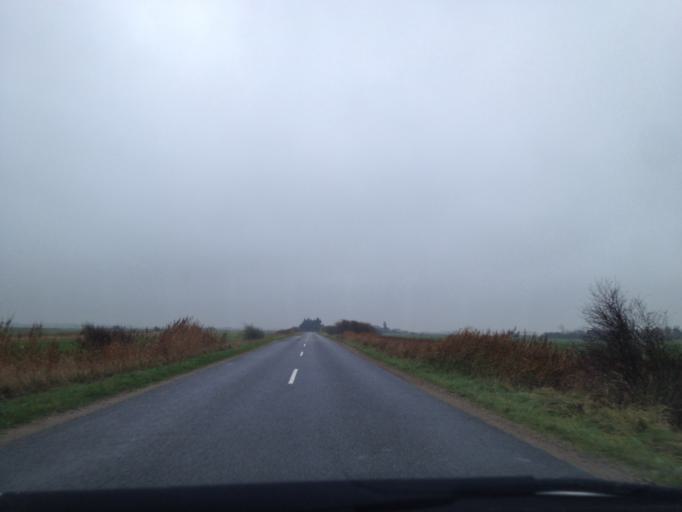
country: DK
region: South Denmark
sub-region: Tonder Kommune
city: Sherrebek
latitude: 55.1125
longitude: 8.7315
